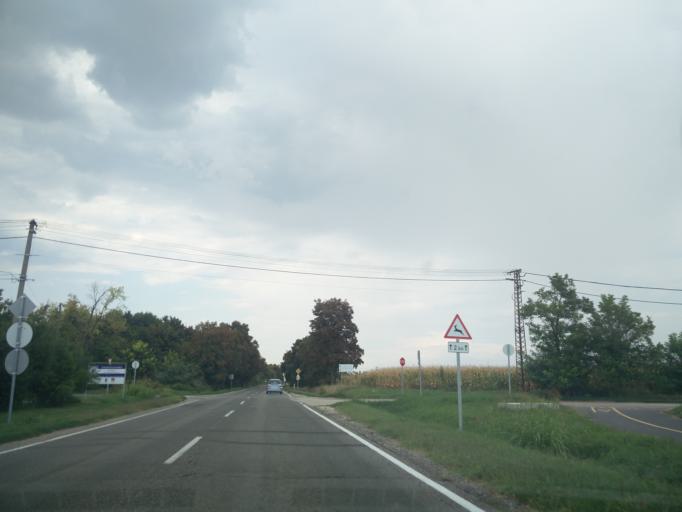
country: HU
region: Fejer
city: Polgardi
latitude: 47.0618
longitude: 18.3083
